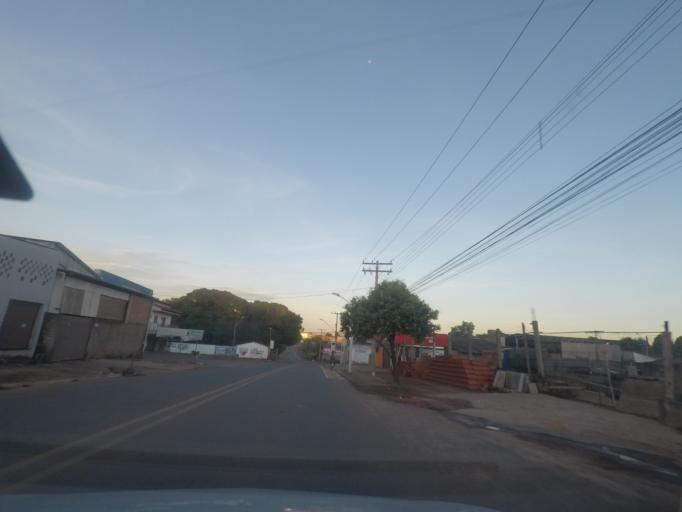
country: BR
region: Goias
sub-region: Goiania
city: Goiania
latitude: -16.6900
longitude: -49.3393
